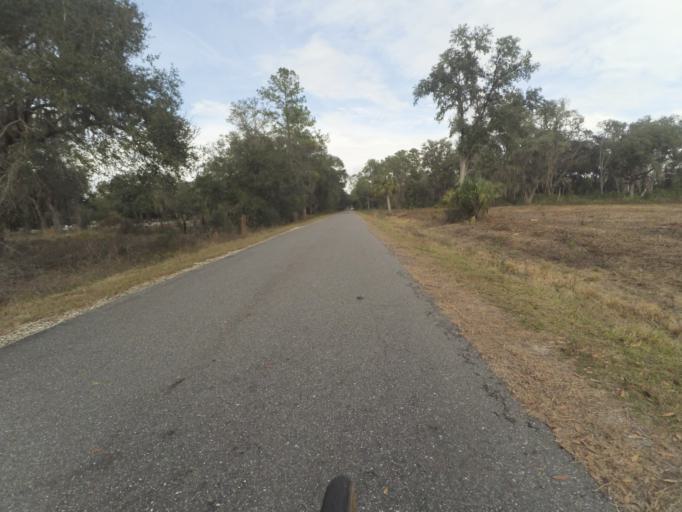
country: US
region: Florida
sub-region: Alachua County
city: Gainesville
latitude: 29.6273
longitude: -82.3111
